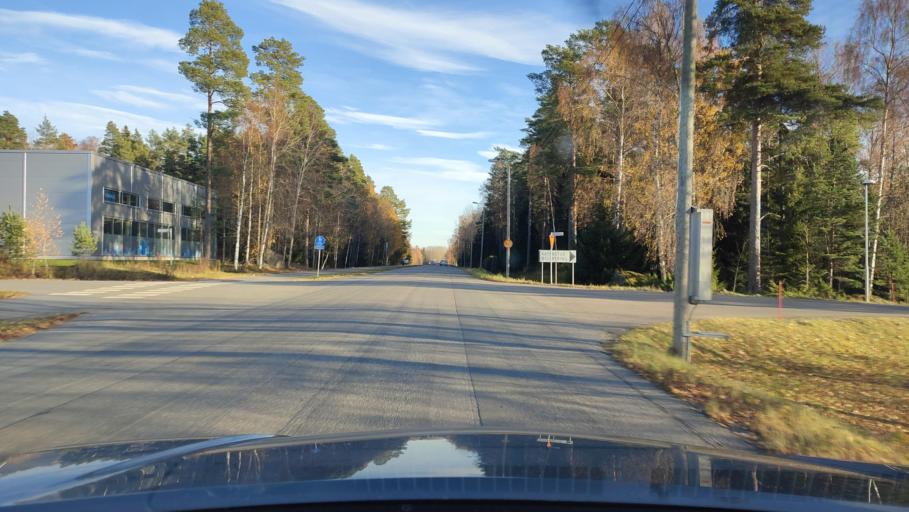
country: FI
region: Ostrobothnia
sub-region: Vaasa
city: Teeriniemi
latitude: 63.0776
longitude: 21.6712
